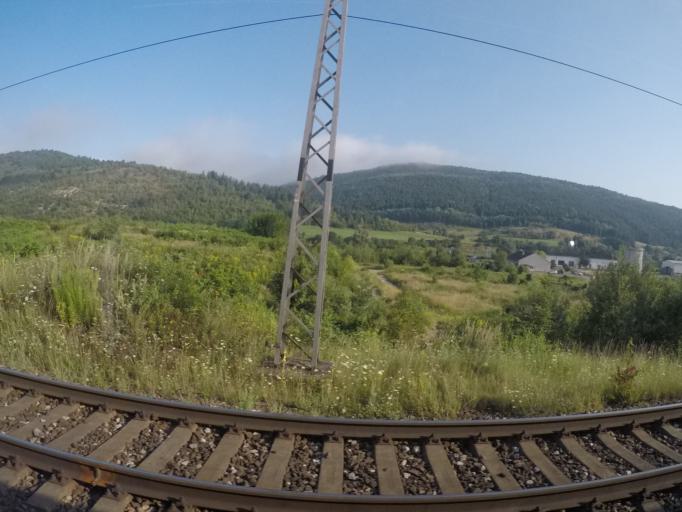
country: SK
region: Kosicky
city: Krompachy
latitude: 48.9234
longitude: 20.8993
